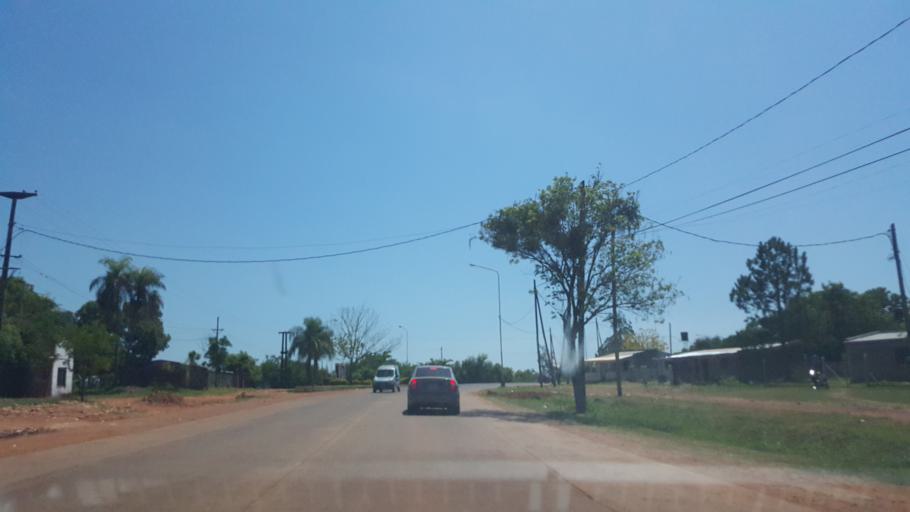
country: AR
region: Corrientes
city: Santo Tome
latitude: -28.5474
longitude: -56.0625
